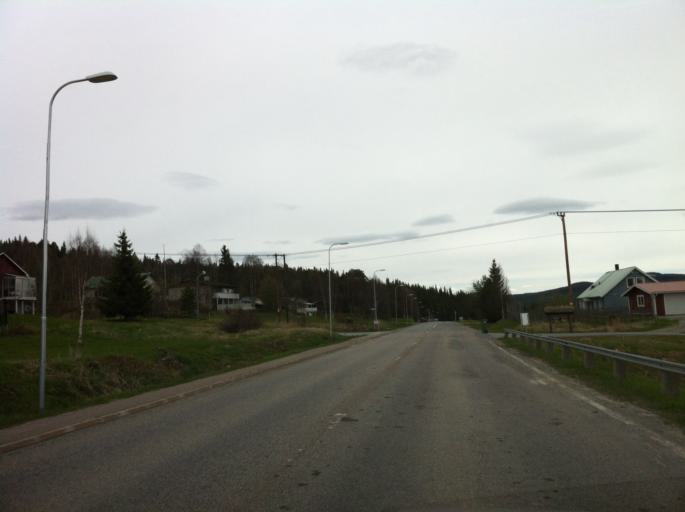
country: NO
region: Hedmark
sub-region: Engerdal
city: Engerdal
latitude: 62.5406
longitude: 12.5499
